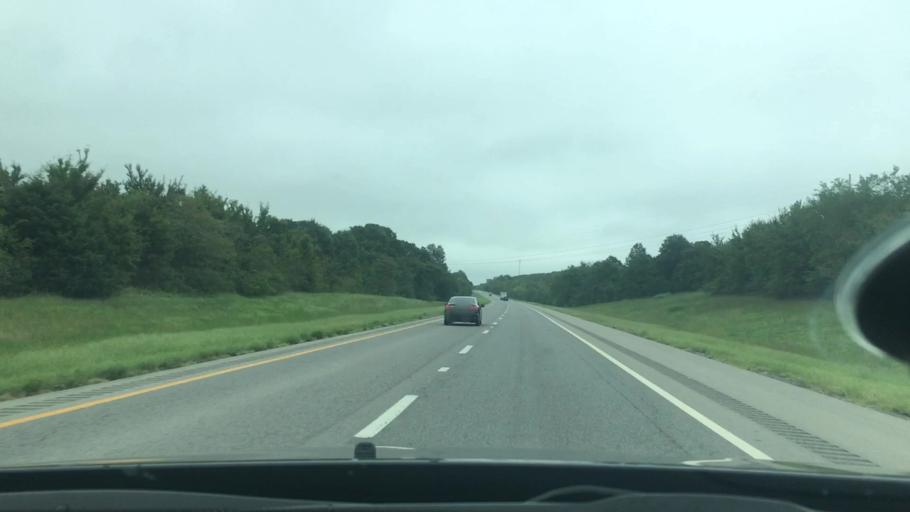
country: US
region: Oklahoma
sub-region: Muskogee County
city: Warner
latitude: 35.4561
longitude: -95.3989
